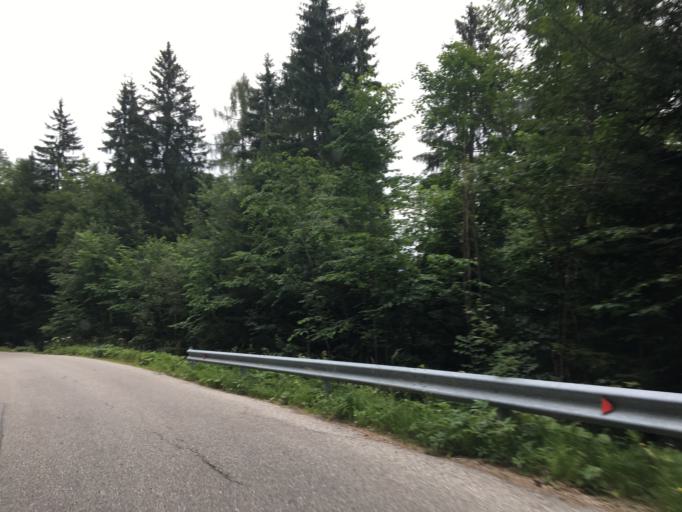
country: AT
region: Salzburg
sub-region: Politischer Bezirk Salzburg-Umgebung
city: Strobl
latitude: 47.6651
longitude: 13.4557
